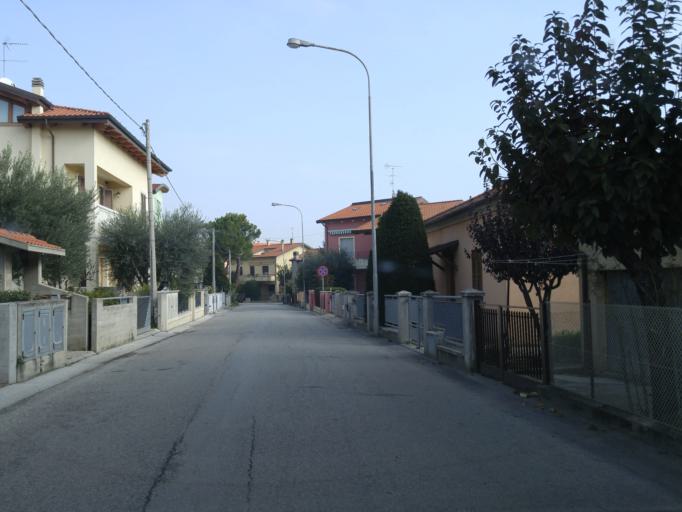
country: IT
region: The Marches
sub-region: Provincia di Pesaro e Urbino
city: Fano
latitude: 43.8279
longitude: 13.0100
